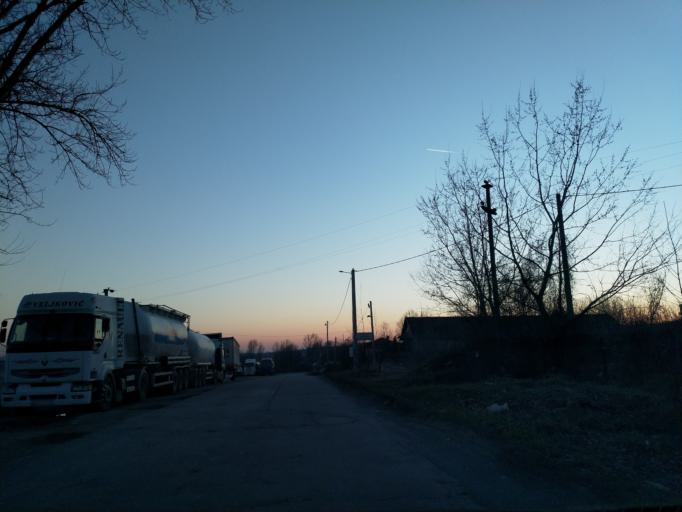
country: RS
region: Central Serbia
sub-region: Pomoravski Okrug
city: Paracin
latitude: 43.9049
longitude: 21.5013
